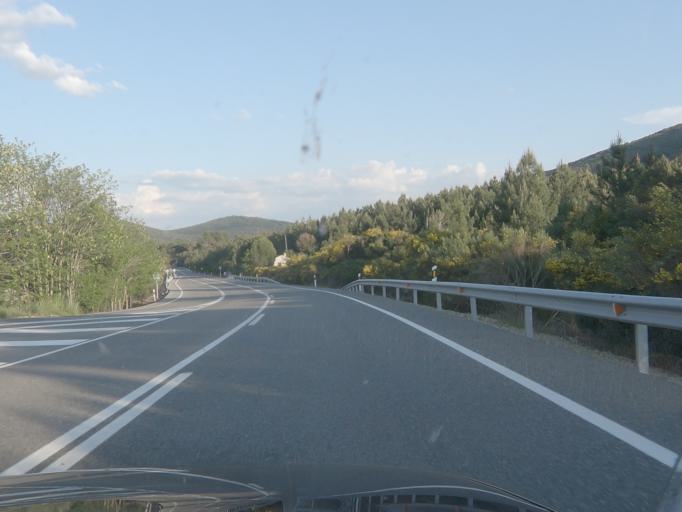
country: PT
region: Portalegre
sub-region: Portalegre
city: Sao Juliao
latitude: 39.3462
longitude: -7.2987
